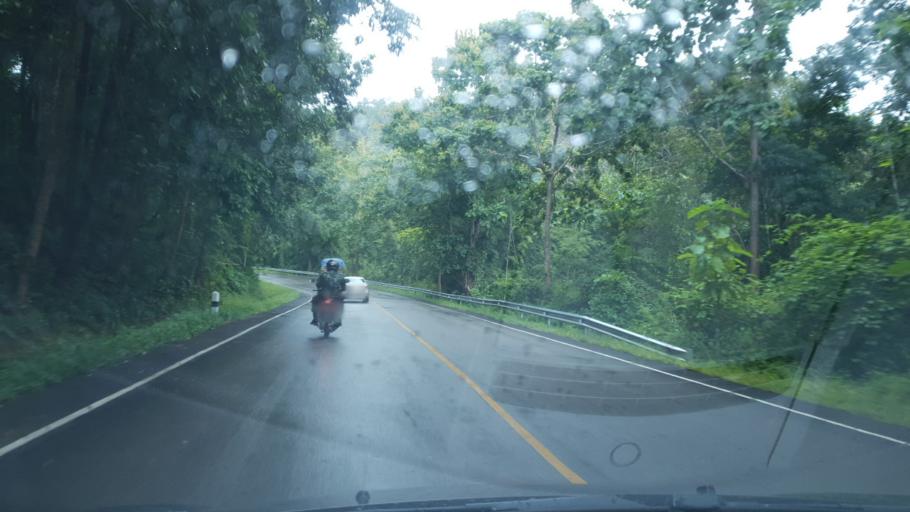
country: TH
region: Mae Hong Son
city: Mae La Noi
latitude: 18.5573
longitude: 97.9251
